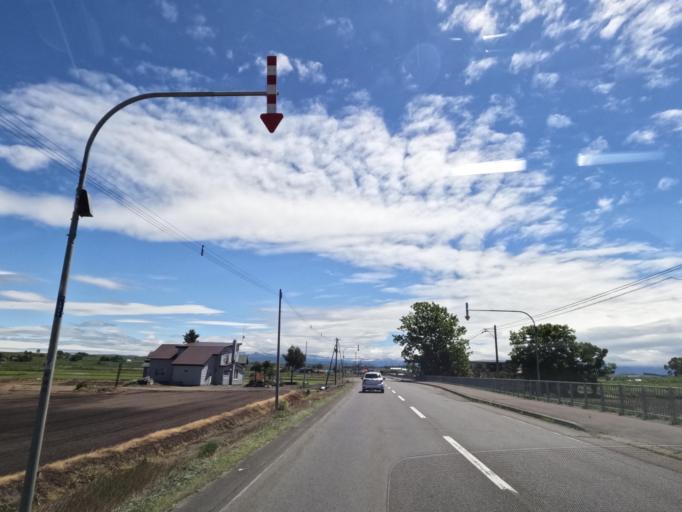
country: JP
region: Hokkaido
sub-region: Asahikawa-shi
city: Asahikawa
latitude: 43.6657
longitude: 142.4119
